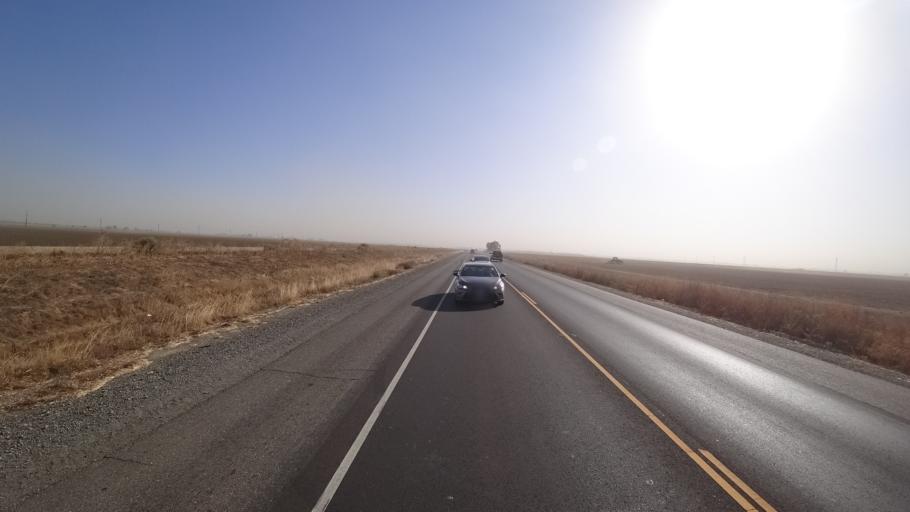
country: US
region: California
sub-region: Yolo County
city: Woodland
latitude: 38.7674
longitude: -121.7288
